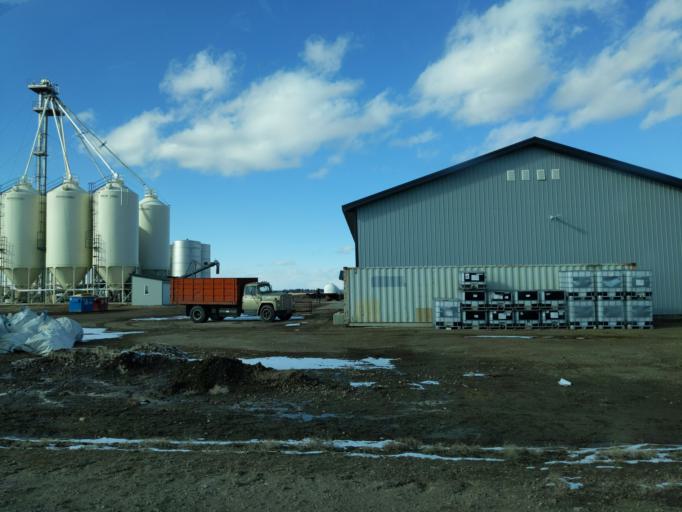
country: CA
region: Saskatchewan
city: Lloydminster
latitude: 53.2440
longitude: -109.9714
